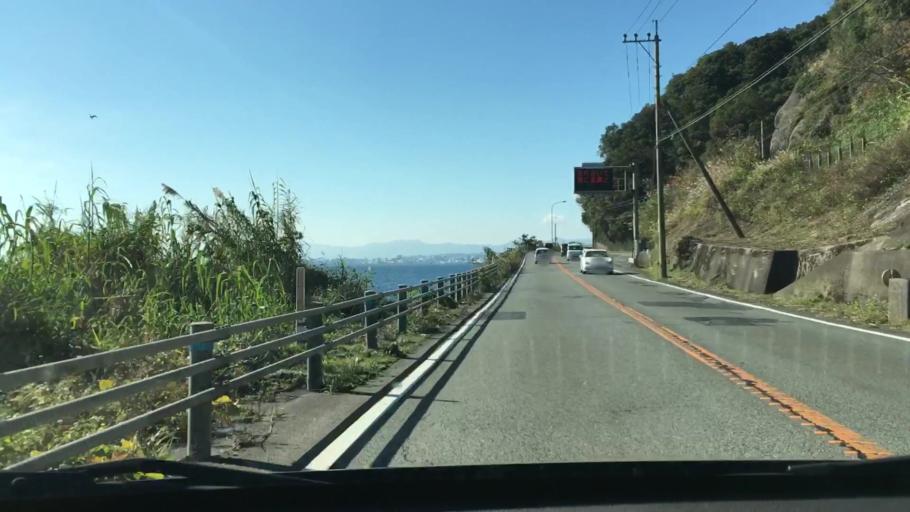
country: JP
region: Kagoshima
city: Kagoshima-shi
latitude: 31.6272
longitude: 130.5961
